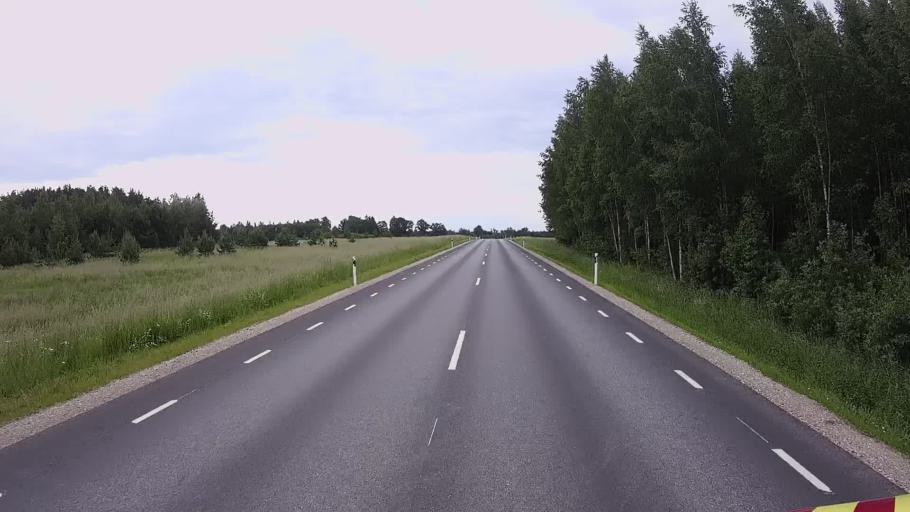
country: EE
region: Viljandimaa
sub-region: Viljandi linn
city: Viljandi
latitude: 58.2350
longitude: 25.5987
